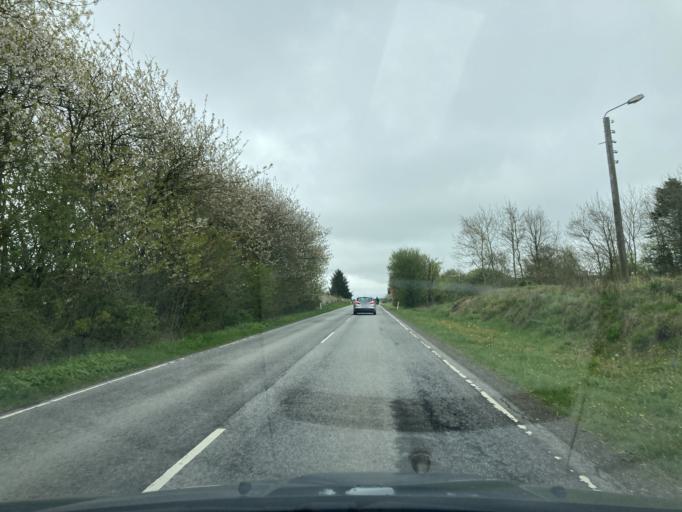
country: DK
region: North Denmark
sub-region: Thisted Kommune
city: Hurup
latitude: 56.8467
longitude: 8.3653
